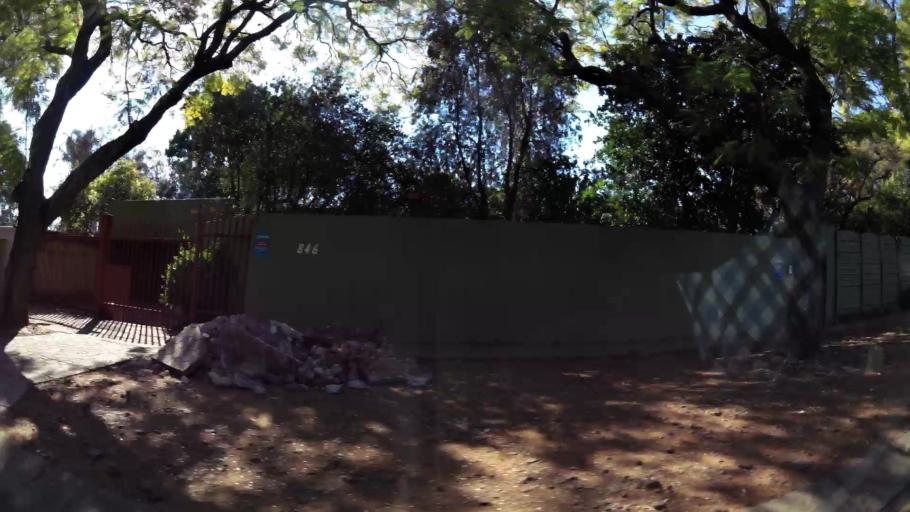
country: ZA
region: Gauteng
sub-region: City of Tshwane Metropolitan Municipality
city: Pretoria
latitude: -25.7660
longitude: 28.2321
